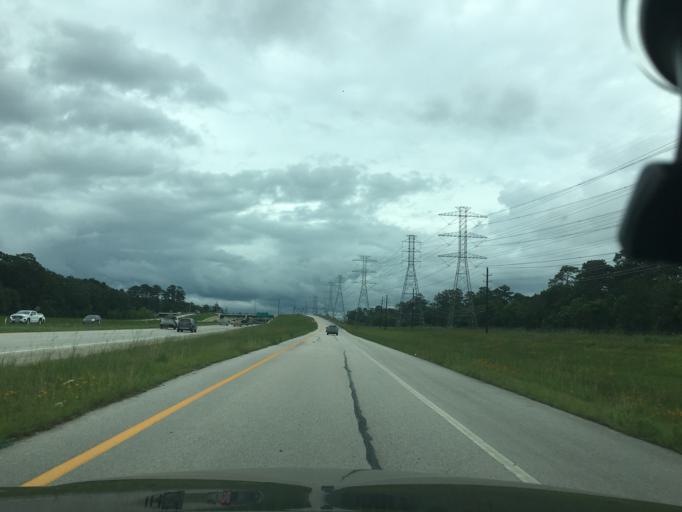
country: US
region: Texas
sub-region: Harris County
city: Spring
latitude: 30.0897
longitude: -95.4621
